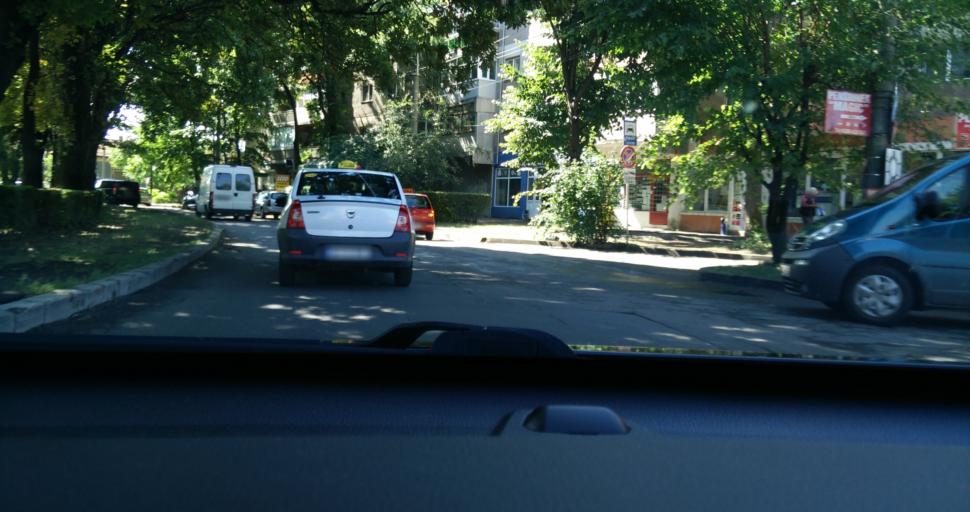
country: RO
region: Bihor
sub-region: Comuna Biharea
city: Oradea
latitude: 47.0436
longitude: 21.9335
